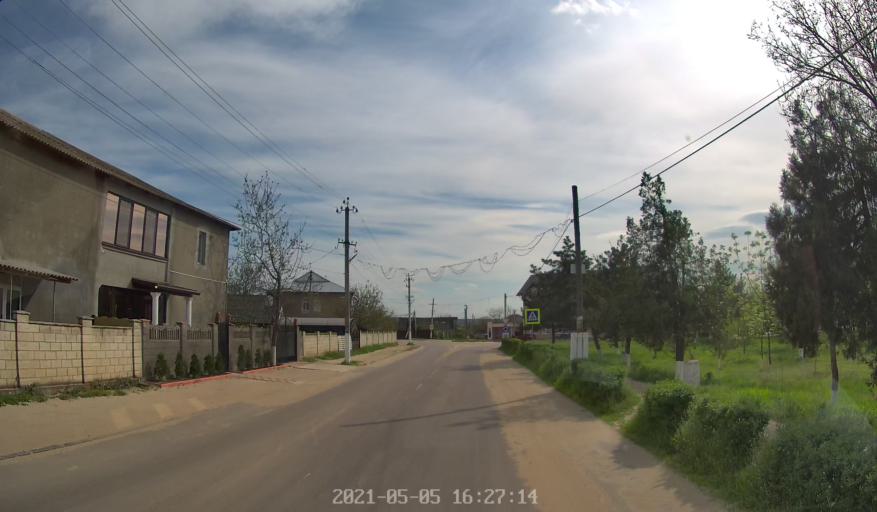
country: MD
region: Criuleni
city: Criuleni
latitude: 47.1285
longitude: 29.1940
